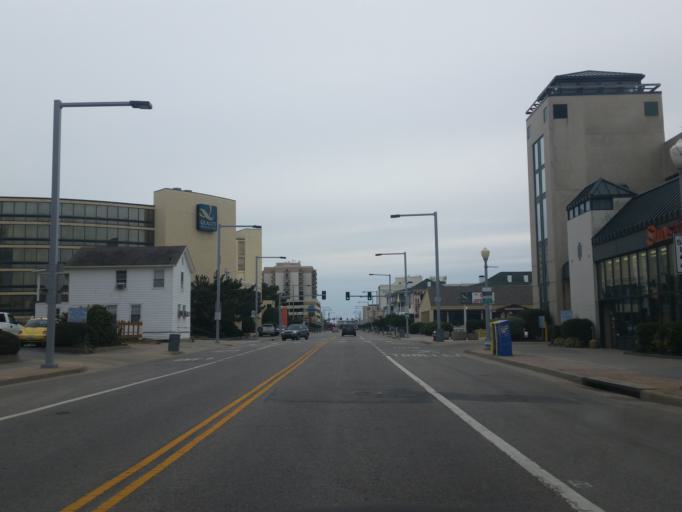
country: US
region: Virginia
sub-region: City of Virginia Beach
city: Virginia Beach
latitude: 36.8372
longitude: -75.9721
